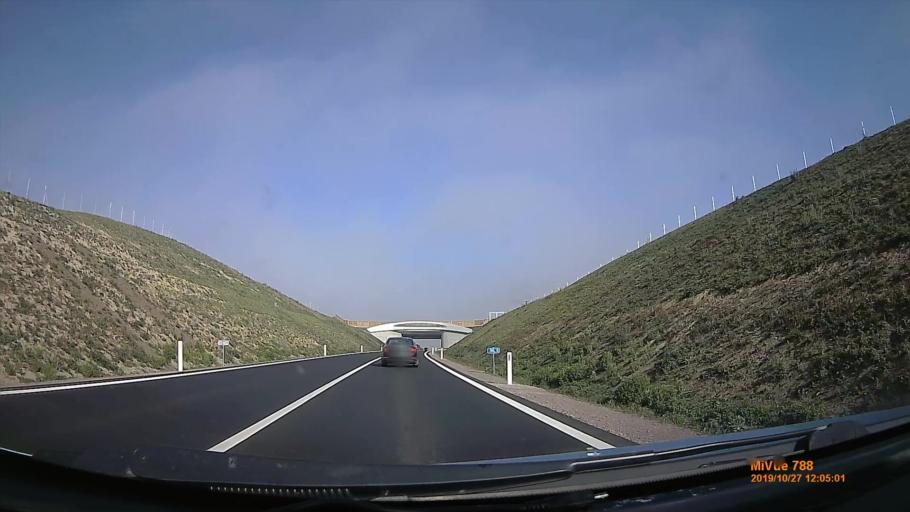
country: AT
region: Lower Austria
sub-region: Politischer Bezirk Mistelbach
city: Drasenhofen
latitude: 48.7591
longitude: 16.6347
